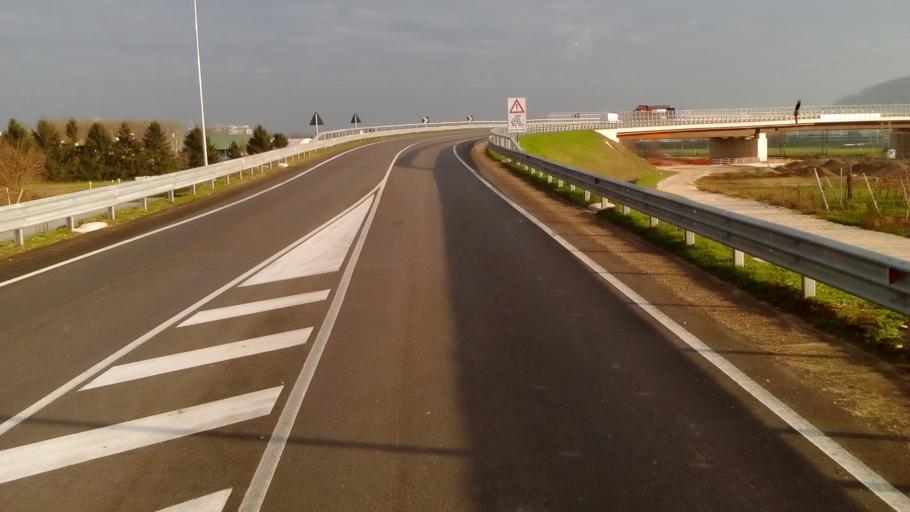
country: IT
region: Veneto
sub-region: Provincia di Vicenza
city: Brendola
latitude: 45.4855
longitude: 11.4302
